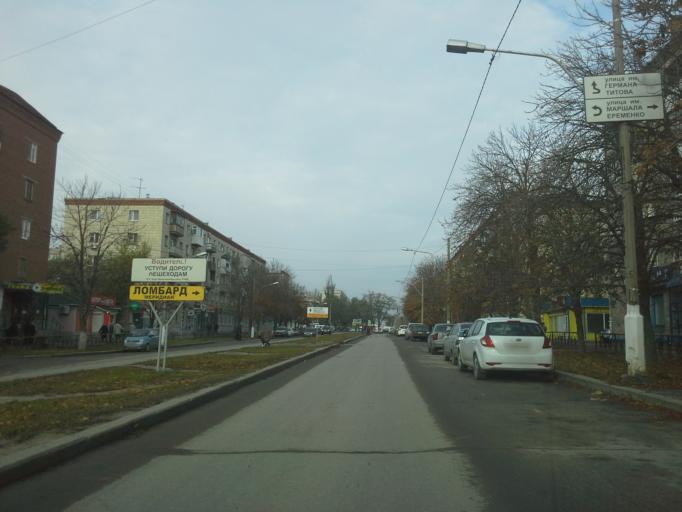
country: RU
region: Volgograd
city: Vodstroy
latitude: 48.7829
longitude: 44.5664
